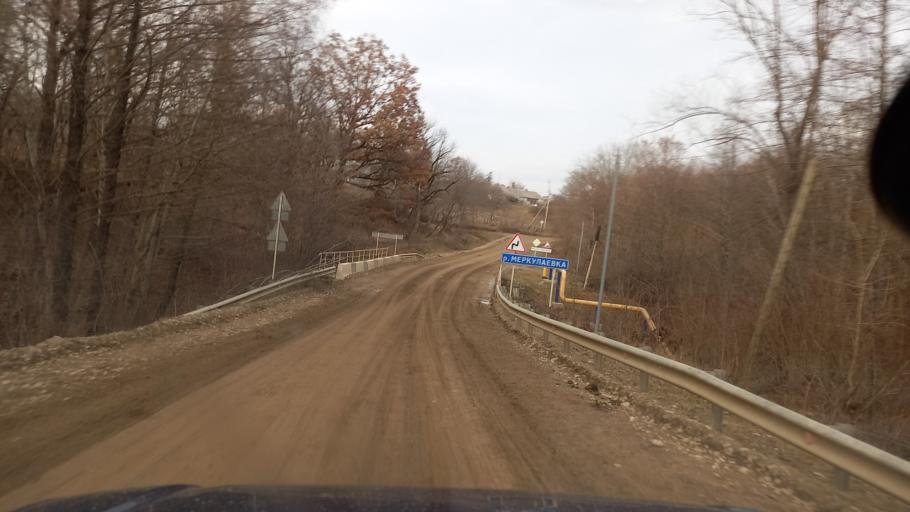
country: RU
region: Adygeya
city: Kamennomostskiy
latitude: 44.1643
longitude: 40.2444
